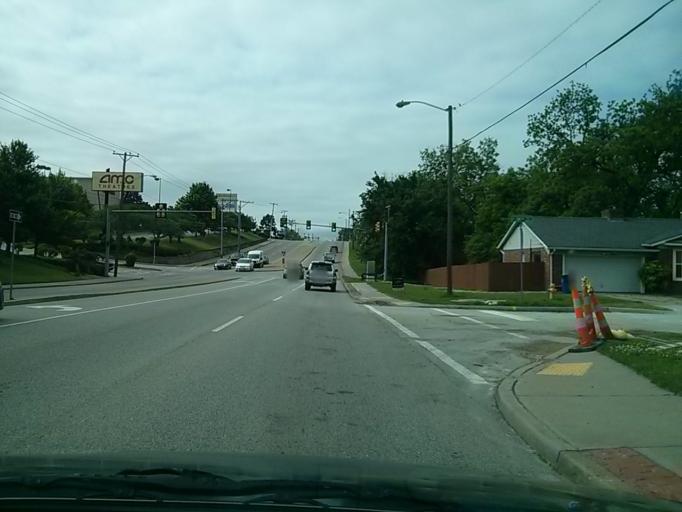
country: US
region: Oklahoma
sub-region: Tulsa County
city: Tulsa
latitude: 36.1075
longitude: -95.9225
